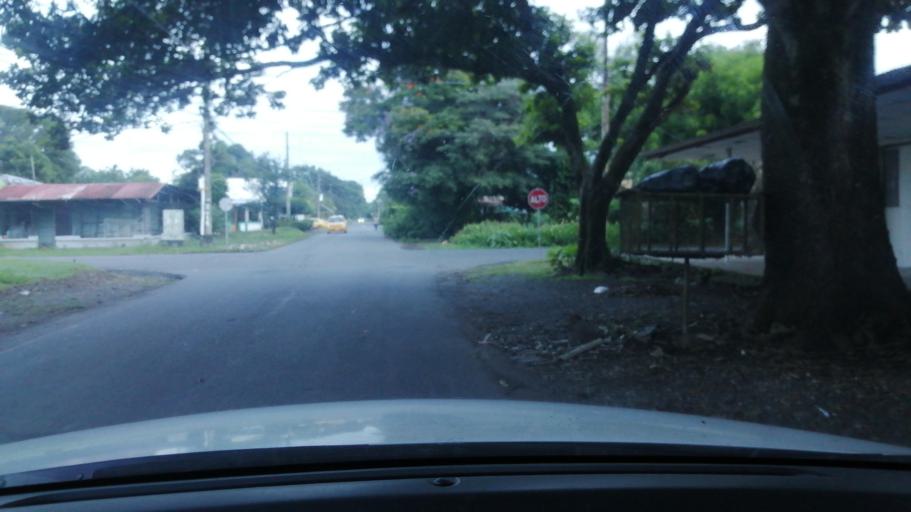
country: PA
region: Chiriqui
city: David
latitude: 8.4279
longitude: -82.4340
